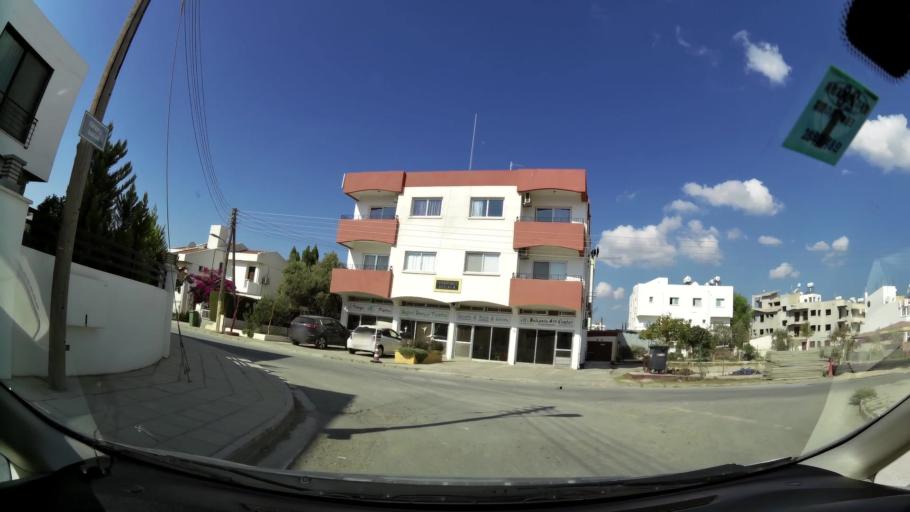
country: CY
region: Lefkosia
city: Nicosia
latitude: 35.2141
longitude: 33.3793
